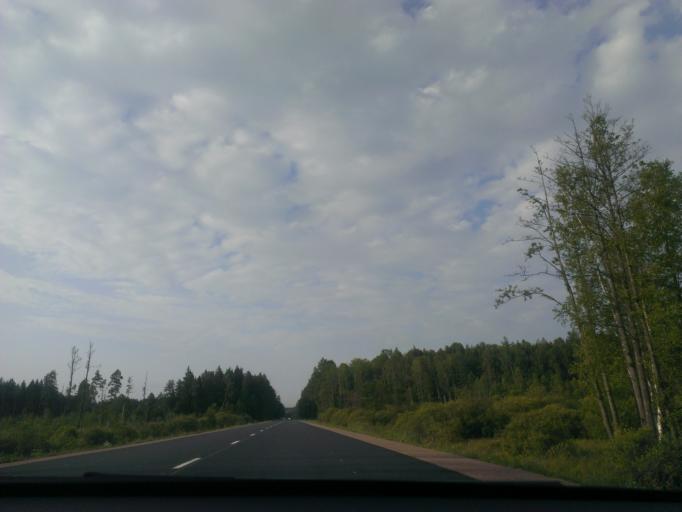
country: LV
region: Lecava
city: Iecava
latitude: 56.7040
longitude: 24.2450
